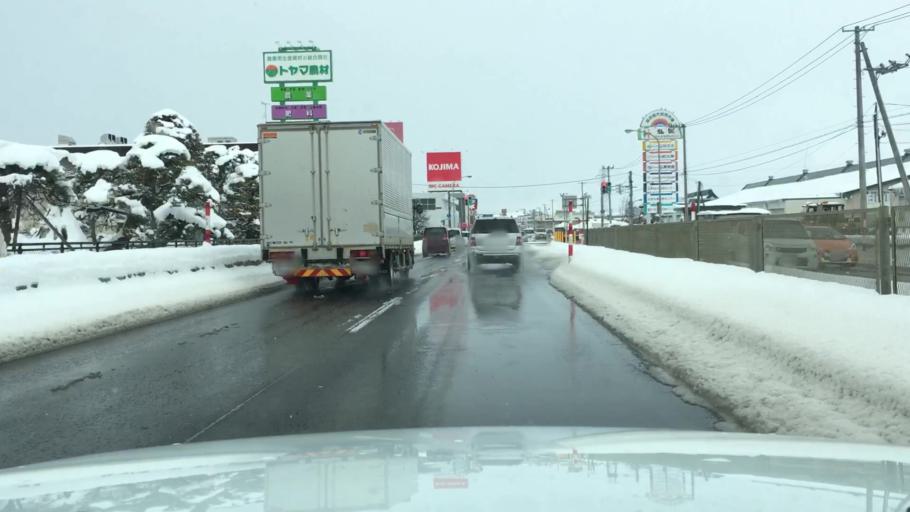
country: JP
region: Aomori
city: Hirosaki
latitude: 40.6054
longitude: 140.4990
